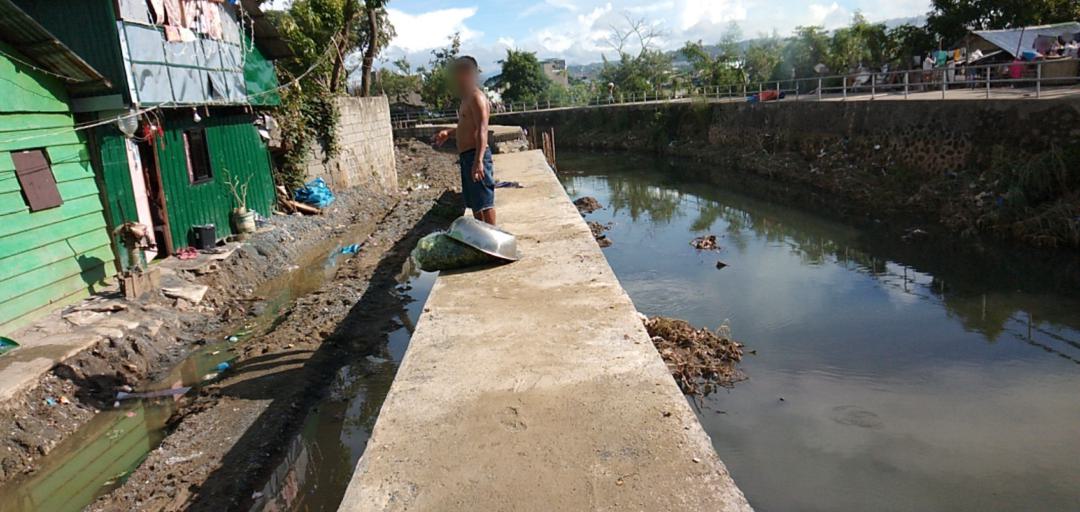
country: PH
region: Calabarzon
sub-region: Province of Rizal
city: Taytay
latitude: 14.5586
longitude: 121.1261
